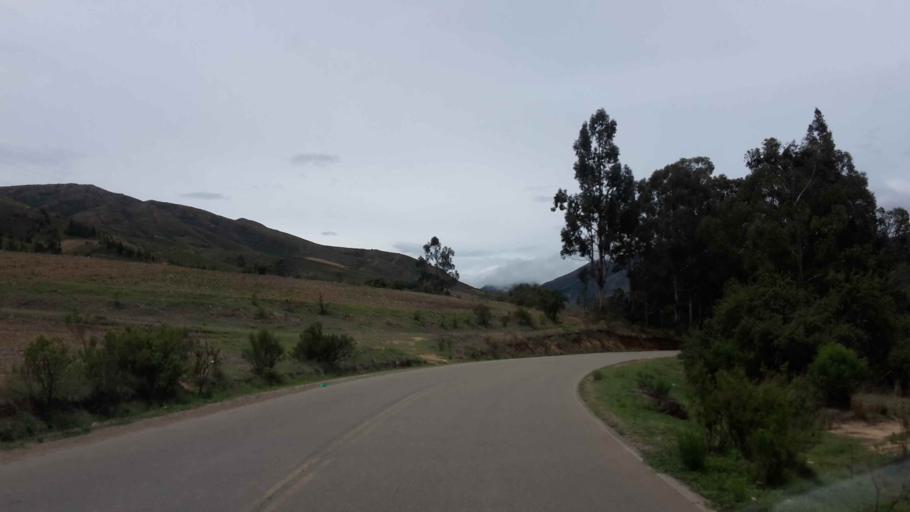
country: BO
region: Cochabamba
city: Totora
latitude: -17.6664
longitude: -65.2238
